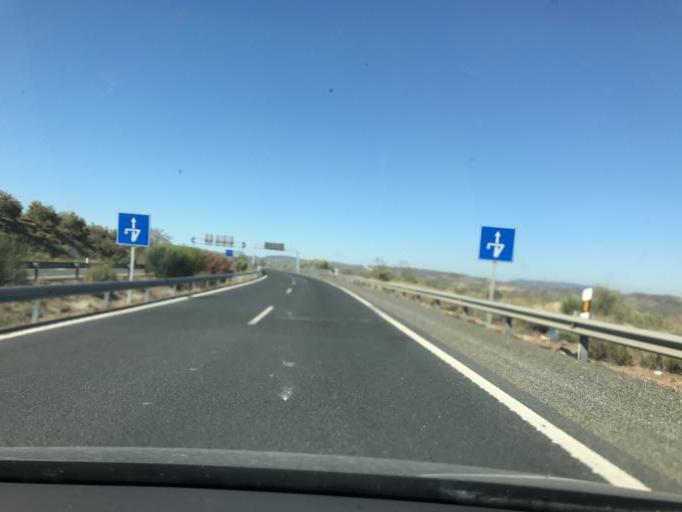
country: ES
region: Andalusia
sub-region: Provincia de Granada
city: Loja
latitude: 37.1663
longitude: -4.1804
